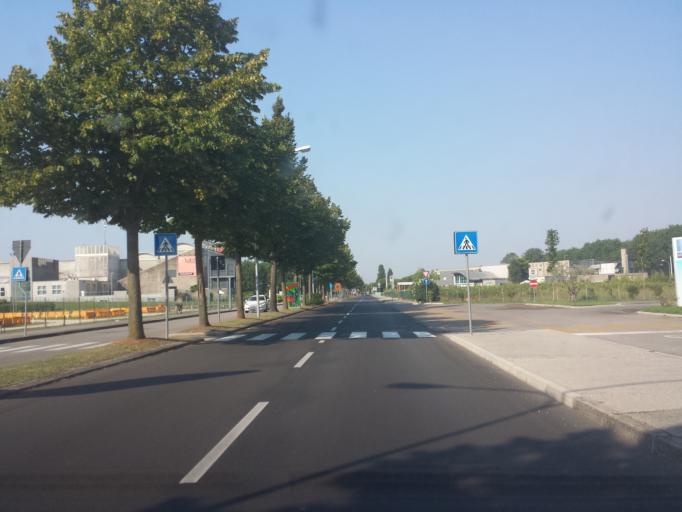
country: IT
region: Veneto
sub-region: Provincia di Venezia
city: Lido di Iesolo
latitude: 45.5041
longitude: 12.6323
